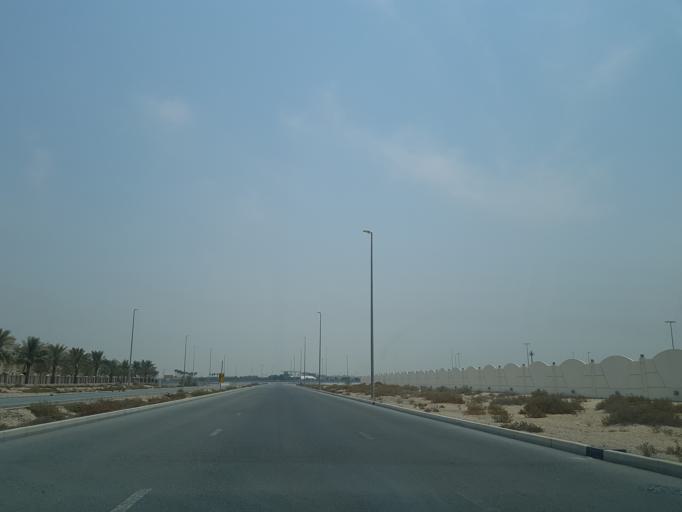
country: AE
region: Dubai
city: Dubai
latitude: 25.0337
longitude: 55.2486
